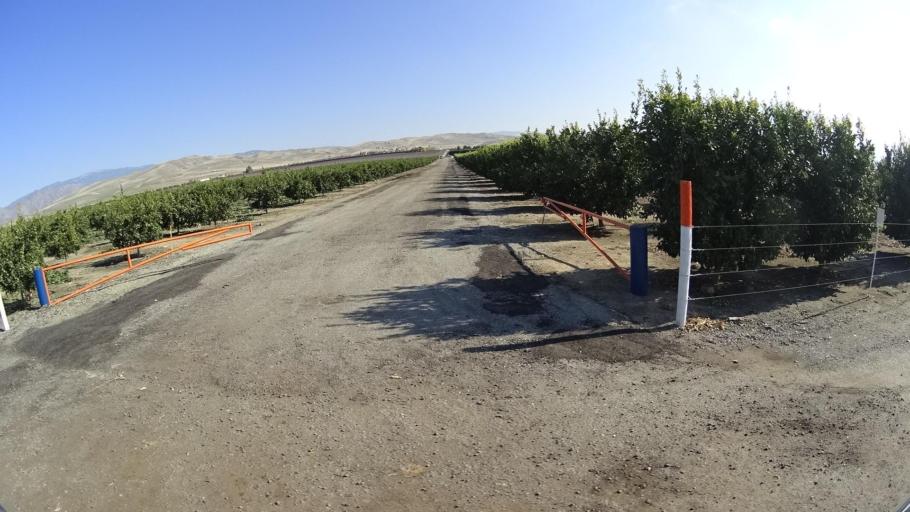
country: US
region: California
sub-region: Kern County
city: Arvin
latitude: 35.2930
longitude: -118.7708
